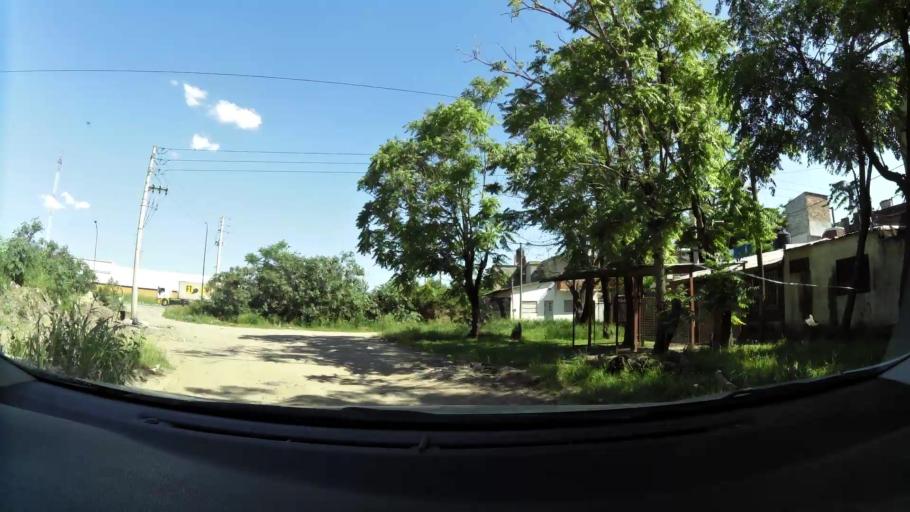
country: AR
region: Buenos Aires F.D.
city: Villa Lugano
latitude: -34.7039
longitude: -58.4697
